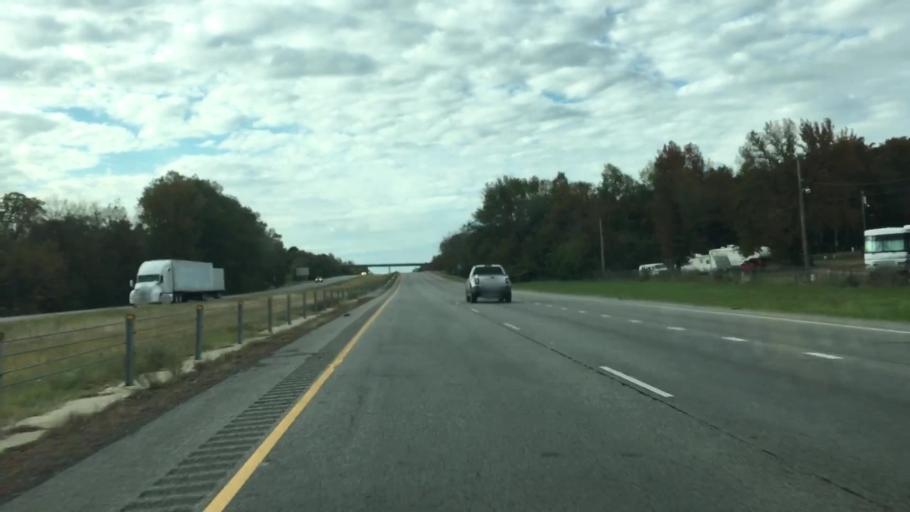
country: US
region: Arkansas
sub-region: Conway County
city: Morrilton
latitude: 35.1770
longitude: -92.7498
